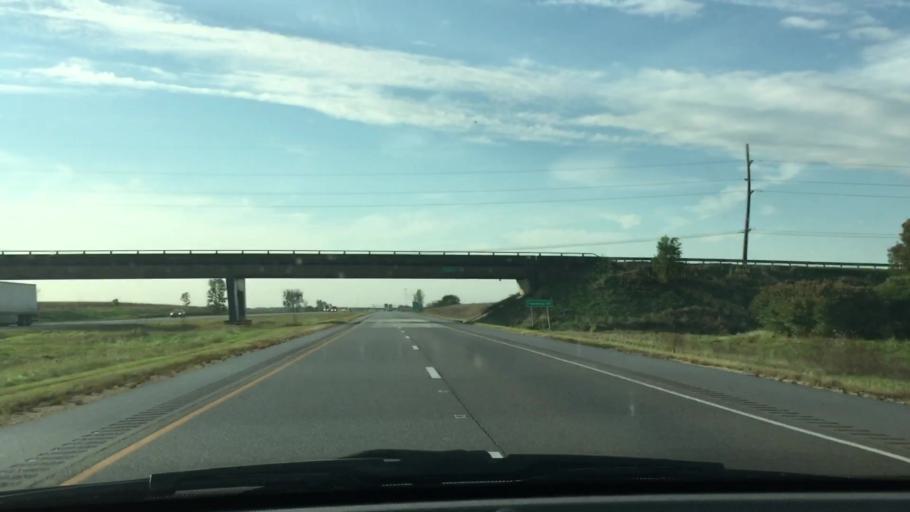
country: US
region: Illinois
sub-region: Ogle County
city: Hillcrest
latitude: 41.9488
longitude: -89.0251
